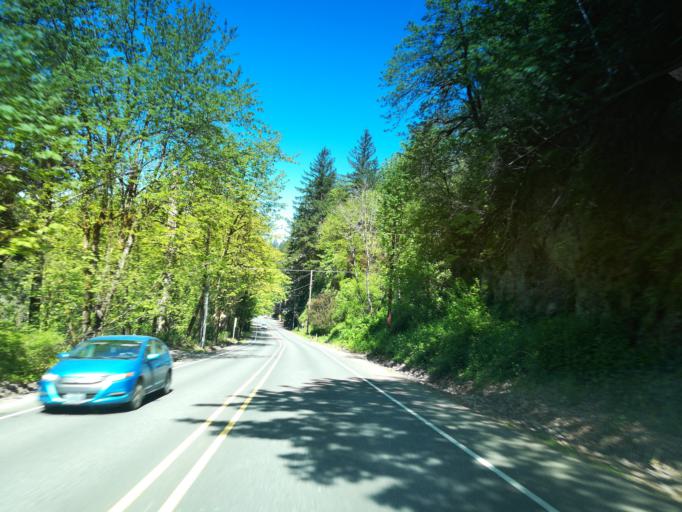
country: US
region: Oregon
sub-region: Multnomah County
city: Troutdale
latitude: 45.5117
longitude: -122.3630
